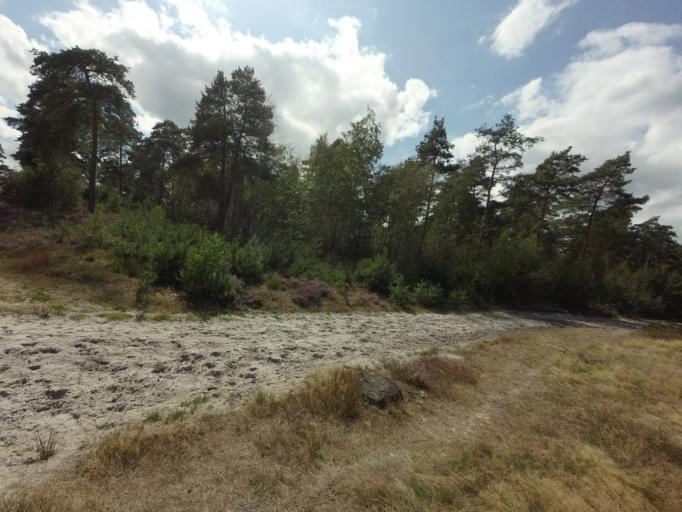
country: NL
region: Limburg
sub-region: Gemeente Brunssum
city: Brunssum
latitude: 50.9236
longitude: 6.0051
